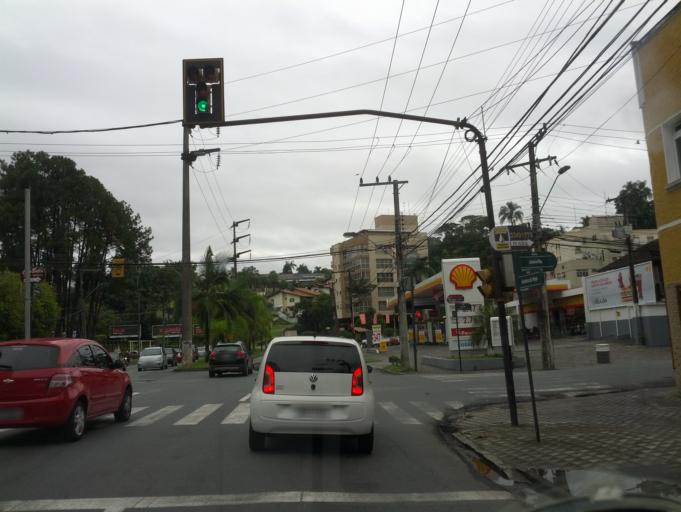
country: BR
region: Santa Catarina
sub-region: Blumenau
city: Blumenau
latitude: -26.9091
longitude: -49.0814
